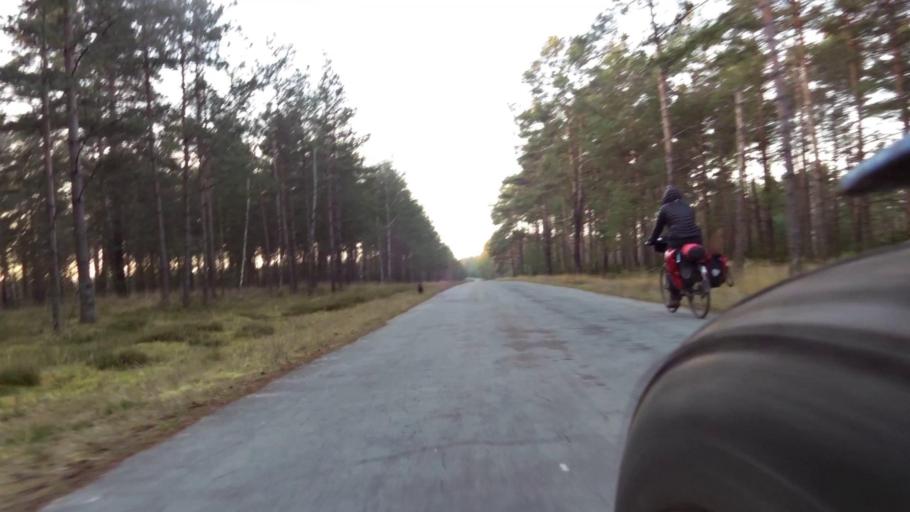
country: PL
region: West Pomeranian Voivodeship
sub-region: Powiat szczecinecki
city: Borne Sulinowo
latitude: 53.5665
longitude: 16.5937
